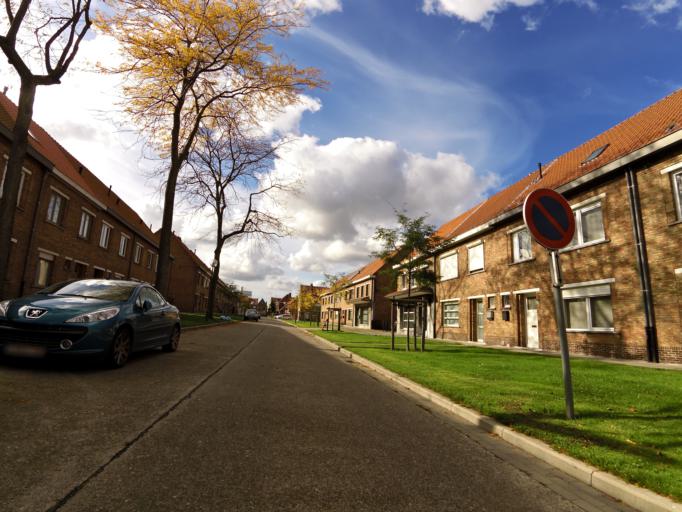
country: BE
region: Flanders
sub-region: Provincie West-Vlaanderen
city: Brugge
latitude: 51.2284
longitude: 3.2304
